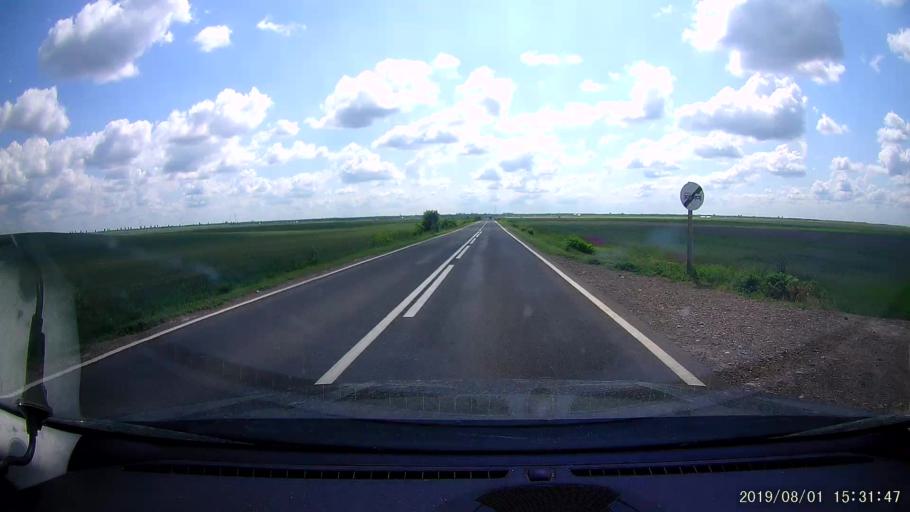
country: RO
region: Braila
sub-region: Comuna Insuratei
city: Insuratei
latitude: 44.9406
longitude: 27.6526
